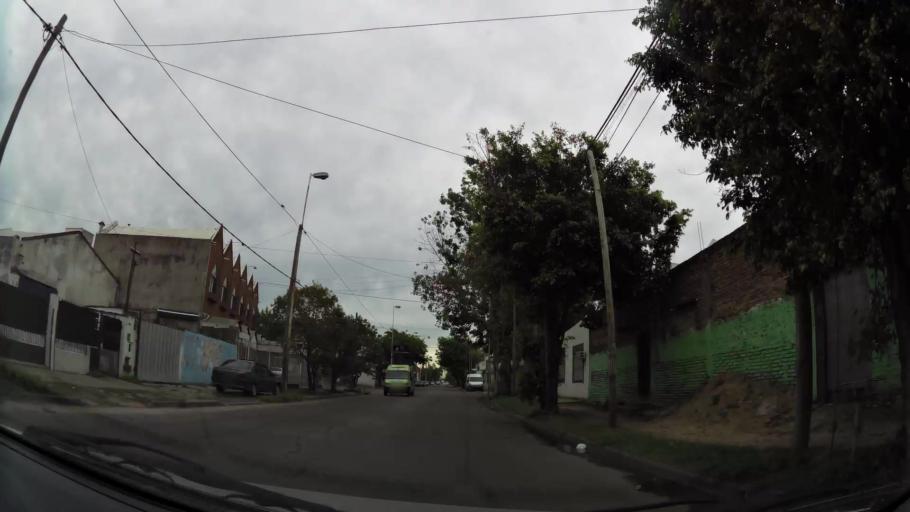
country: AR
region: Buenos Aires
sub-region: Partido de Lanus
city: Lanus
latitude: -34.6922
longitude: -58.3736
